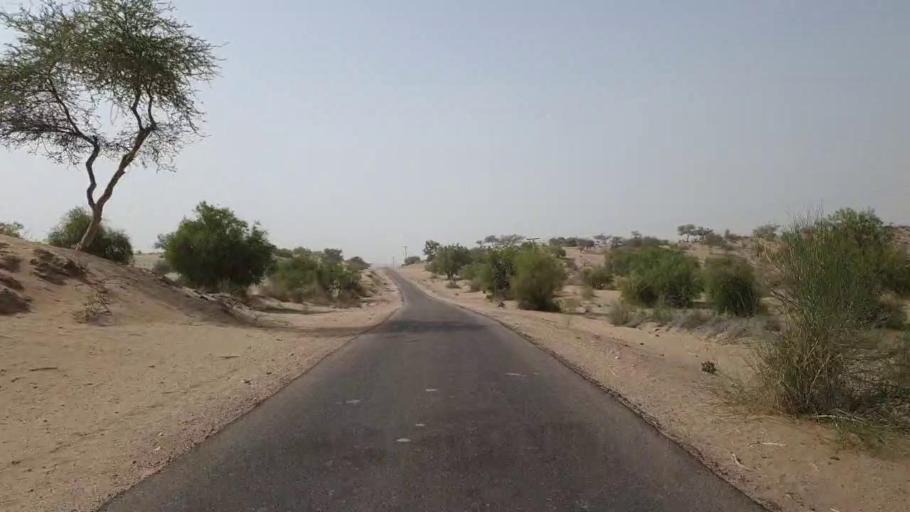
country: PK
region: Sindh
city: Mithi
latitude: 24.5966
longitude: 69.9249
